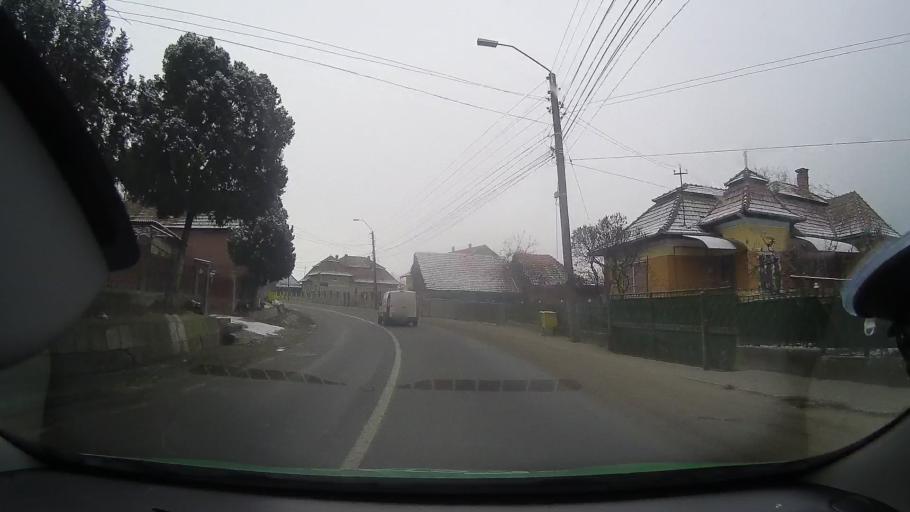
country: RO
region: Cluj
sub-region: Comuna Moldovenesti
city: Moldovenesti
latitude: 46.5252
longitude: 23.6942
